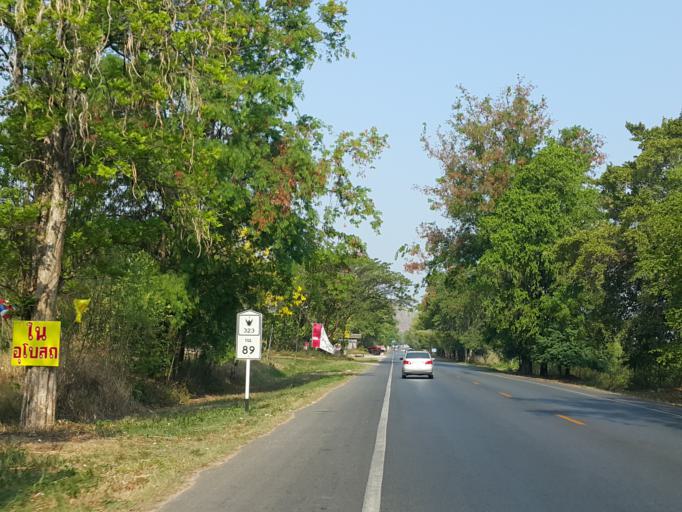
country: TH
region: Kanchanaburi
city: Sai Yok
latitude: 14.0898
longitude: 99.2900
